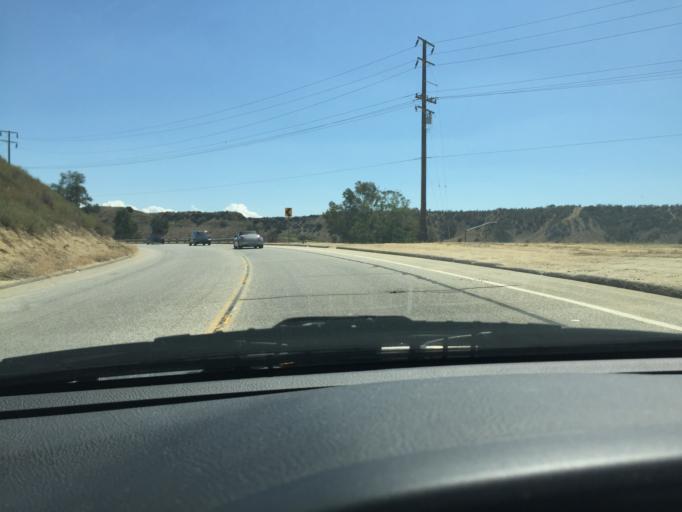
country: US
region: California
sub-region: Riverside County
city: Calimesa
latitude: 34.0167
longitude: -117.0933
